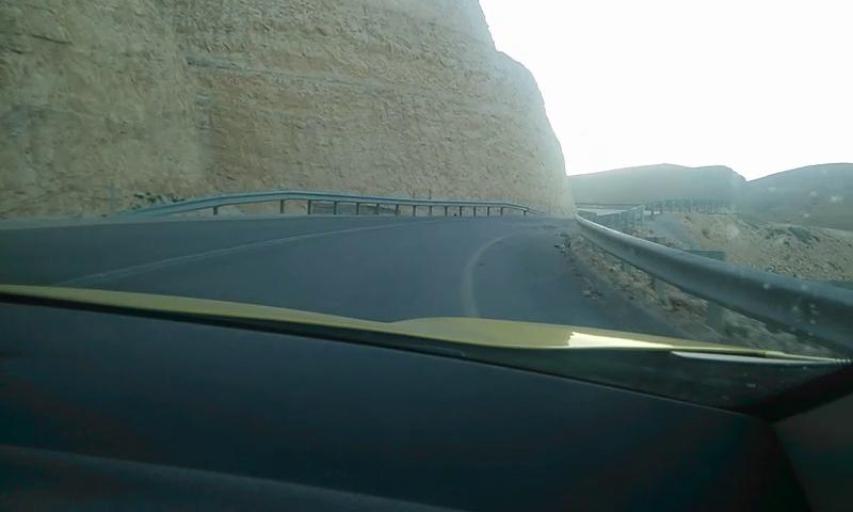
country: PS
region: West Bank
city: An Nuway`imah
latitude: 31.9106
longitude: 35.3748
